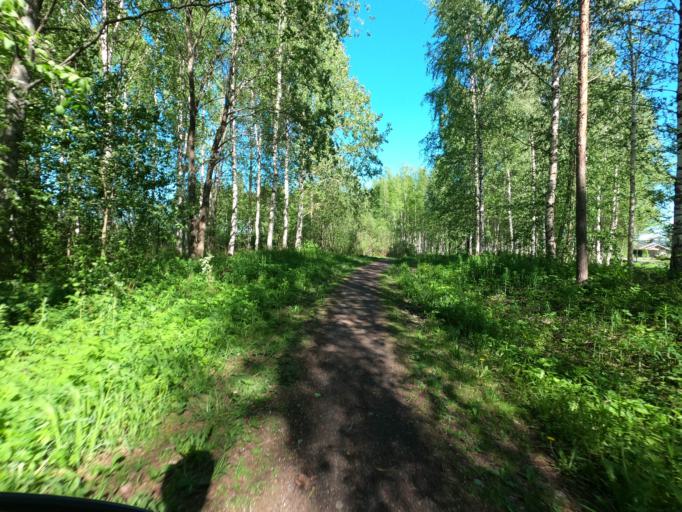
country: FI
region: North Karelia
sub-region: Joensuu
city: Joensuu
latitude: 62.6048
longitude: 29.8212
